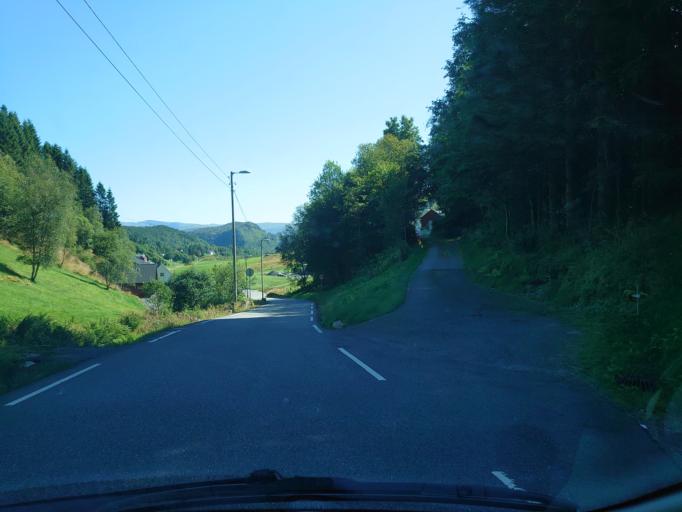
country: NO
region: Hordaland
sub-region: Bergen
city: Hylkje
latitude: 60.4667
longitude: 5.3763
